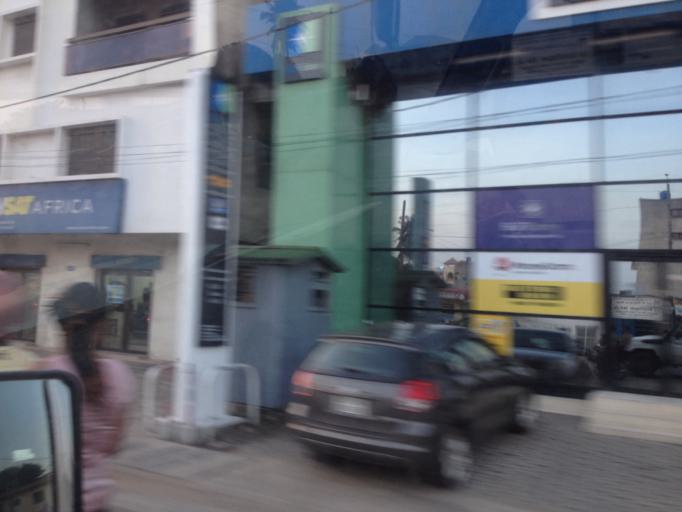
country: BJ
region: Littoral
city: Cotonou
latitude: 6.3720
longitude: 2.4455
